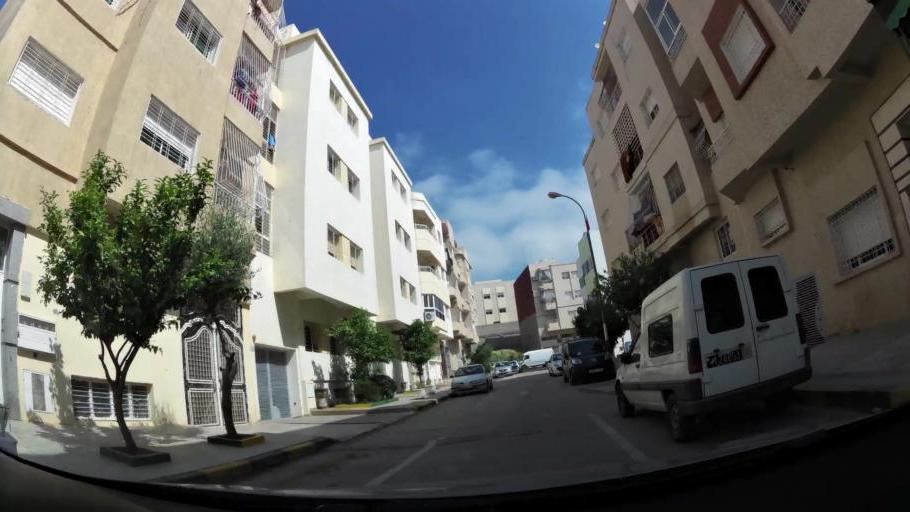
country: MA
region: Fes-Boulemane
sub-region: Fes
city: Fes
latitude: 34.0570
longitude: -5.0303
